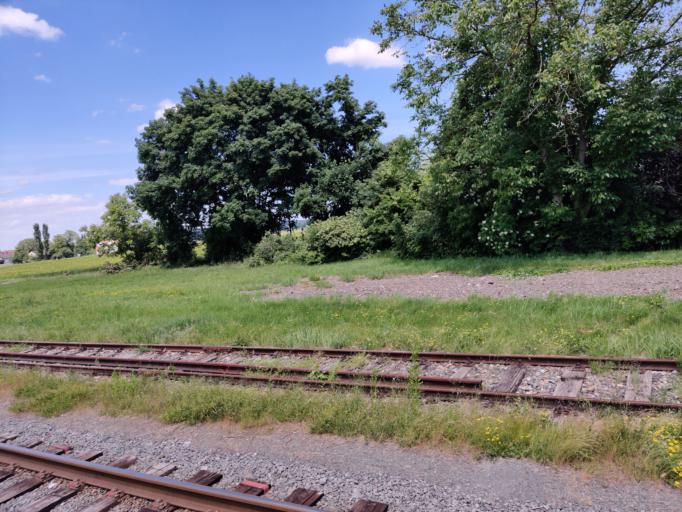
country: AT
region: Styria
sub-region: Politischer Bezirk Suedoststeiermark
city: Bad Radkersburg
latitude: 46.7001
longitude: 15.9930
